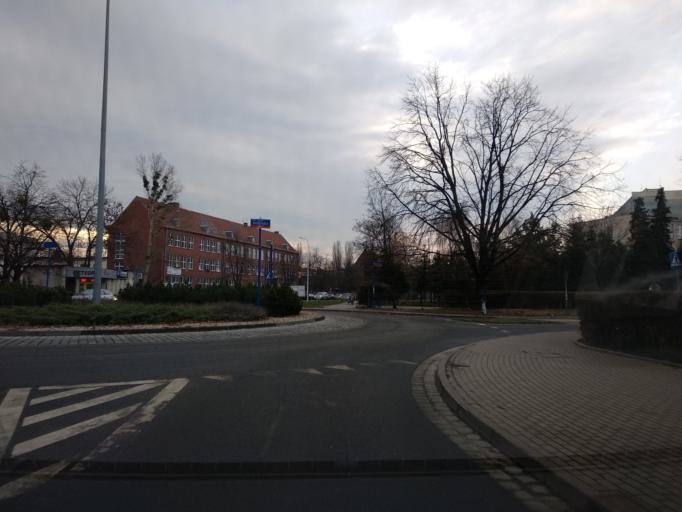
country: PL
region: Lower Silesian Voivodeship
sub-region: Powiat wroclawski
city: Wroclaw
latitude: 51.0951
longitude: 16.9869
